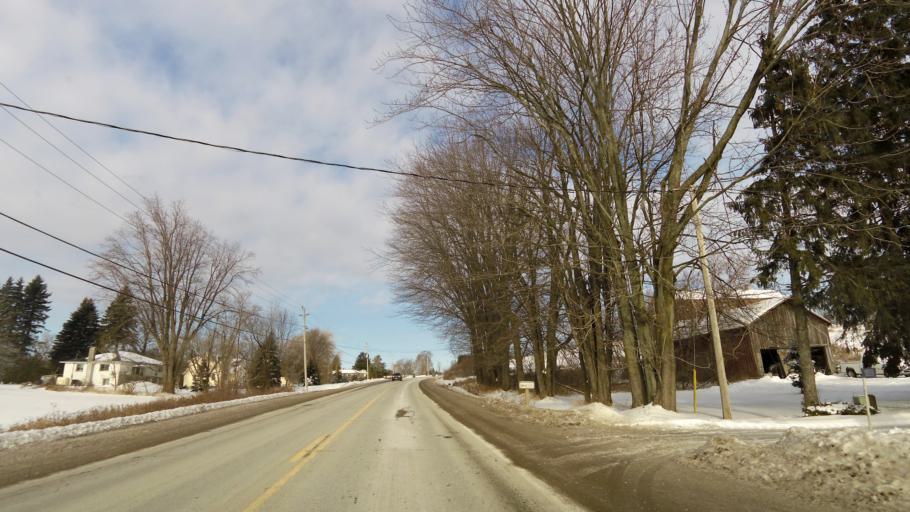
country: CA
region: Ontario
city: Quinte West
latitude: 44.0805
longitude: -77.7731
